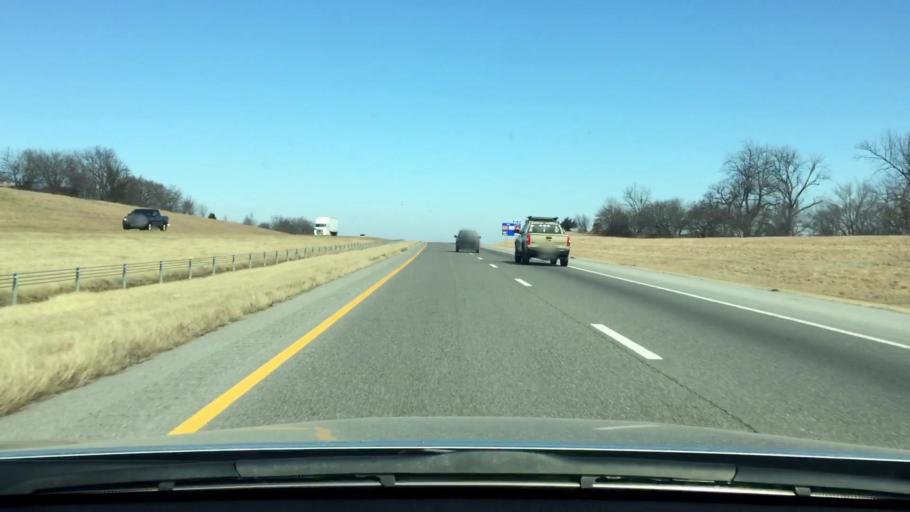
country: US
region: Oklahoma
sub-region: McClain County
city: Purcell
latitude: 34.9588
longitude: -97.3690
